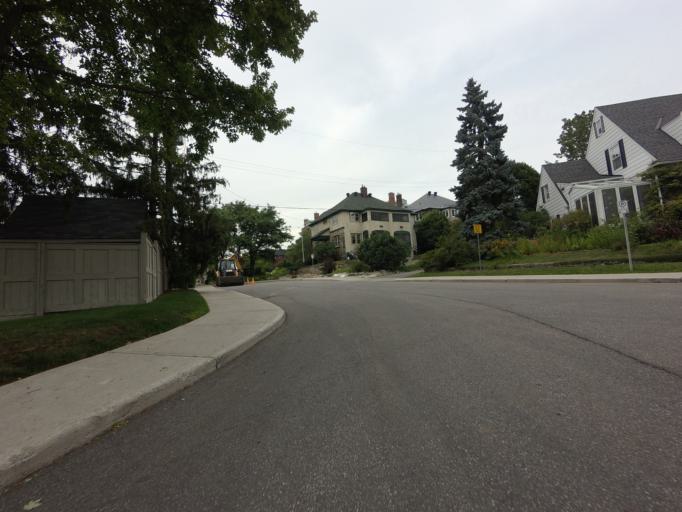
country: CA
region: Ontario
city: Ottawa
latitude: 45.3996
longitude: -75.7016
